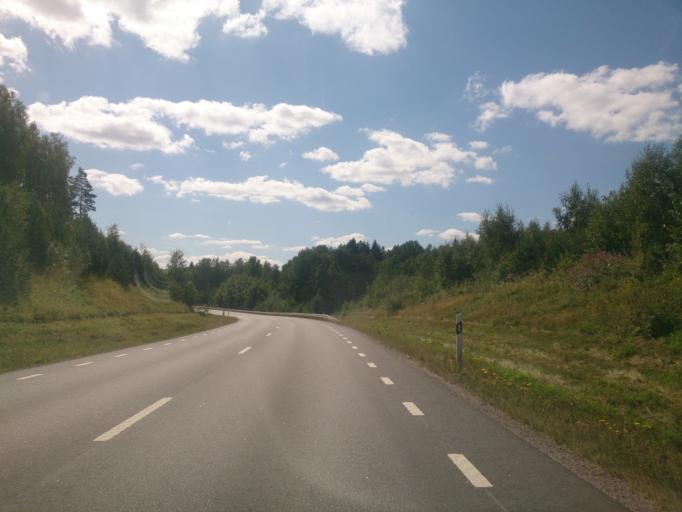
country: SE
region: OEstergoetland
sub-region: Atvidabergs Kommun
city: Atvidaberg
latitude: 58.1869
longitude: 16.0233
